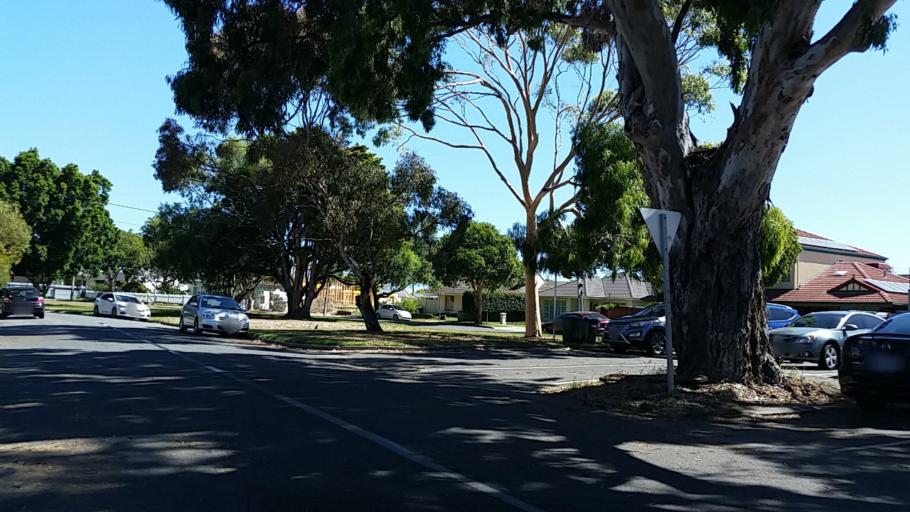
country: AU
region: South Australia
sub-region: Charles Sturt
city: Henley Beach
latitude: -34.9255
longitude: 138.5016
